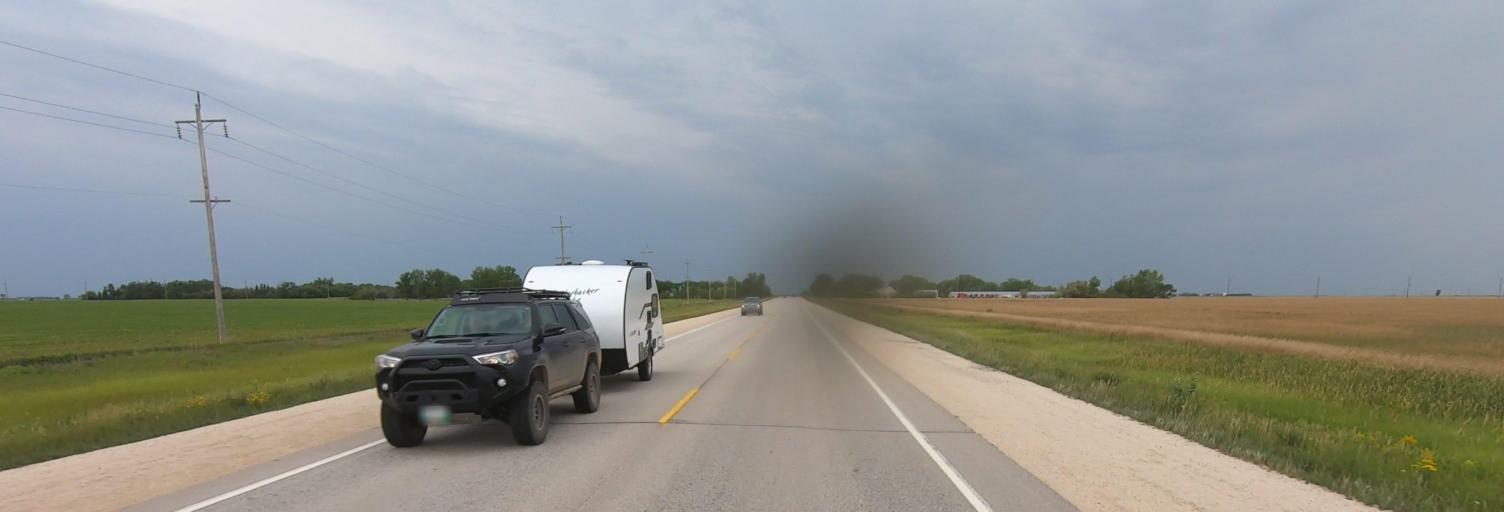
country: CA
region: Manitoba
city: Headingley
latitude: 49.7685
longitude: -97.3591
